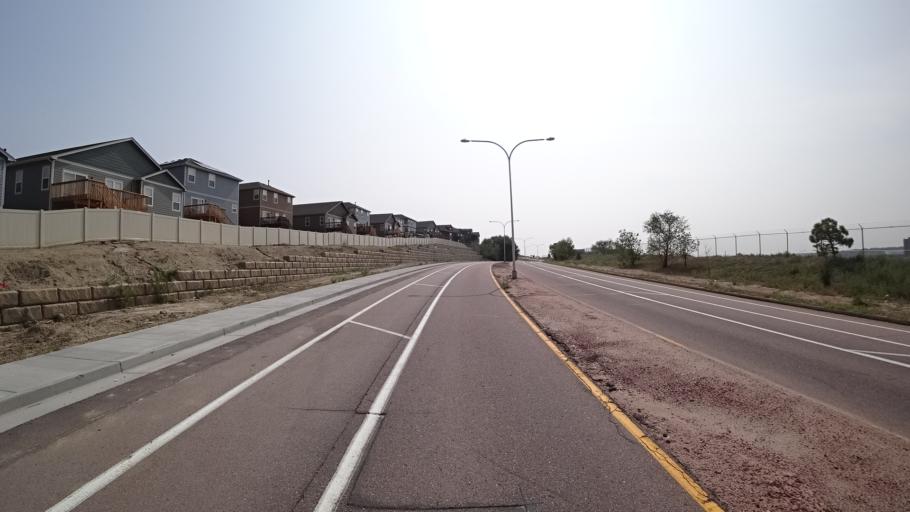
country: US
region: Colorado
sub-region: El Paso County
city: Stratmoor
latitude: 38.8081
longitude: -104.7919
